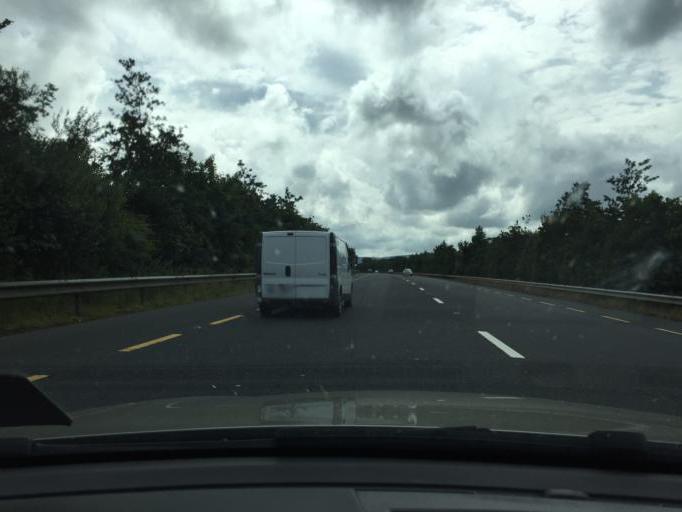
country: IE
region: Munster
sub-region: Waterford
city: Dungarvan
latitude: 52.1860
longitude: -7.4802
